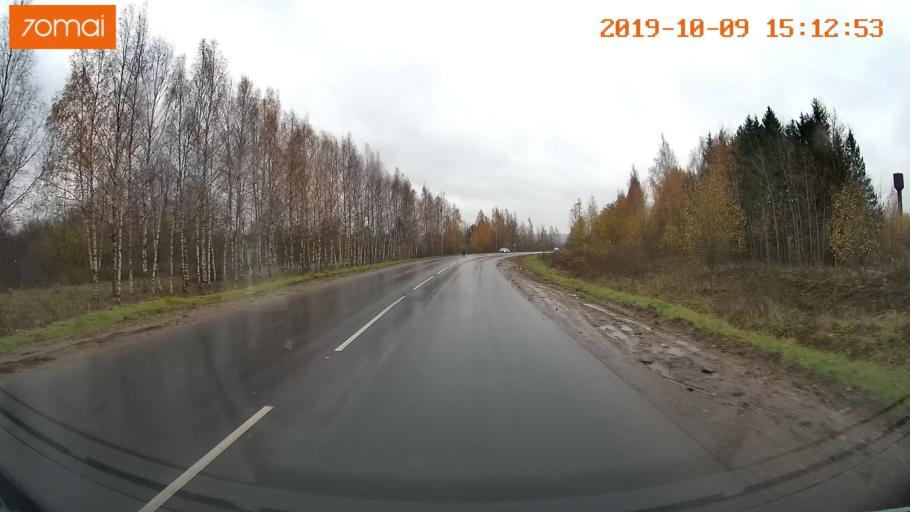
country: RU
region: Kostroma
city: Susanino
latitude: 58.1524
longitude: 41.6142
